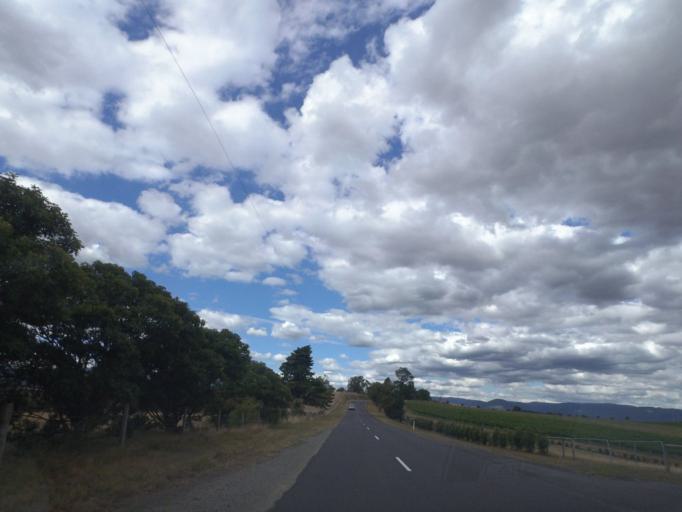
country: AU
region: Victoria
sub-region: Yarra Ranges
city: Yarra Glen
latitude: -37.6437
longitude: 145.4124
